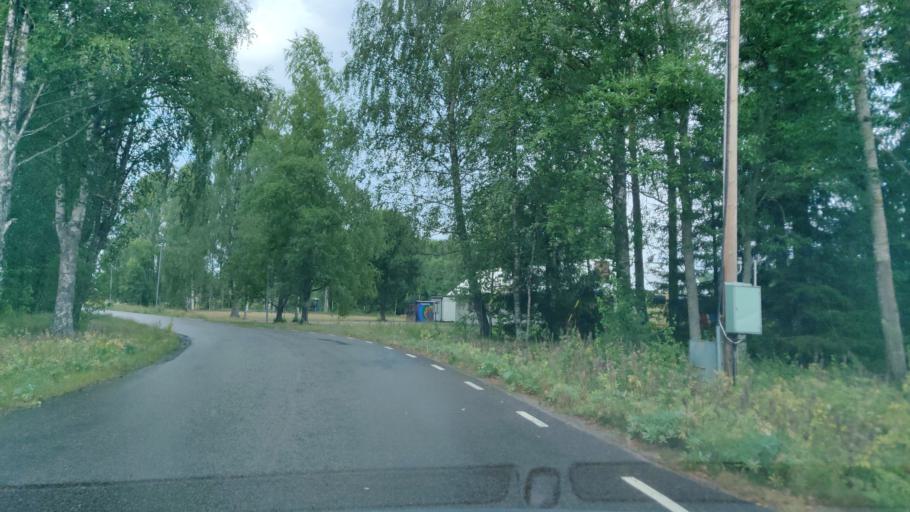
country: SE
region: Vaermland
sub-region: Munkfors Kommun
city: Munkfors
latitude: 59.8519
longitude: 13.5537
